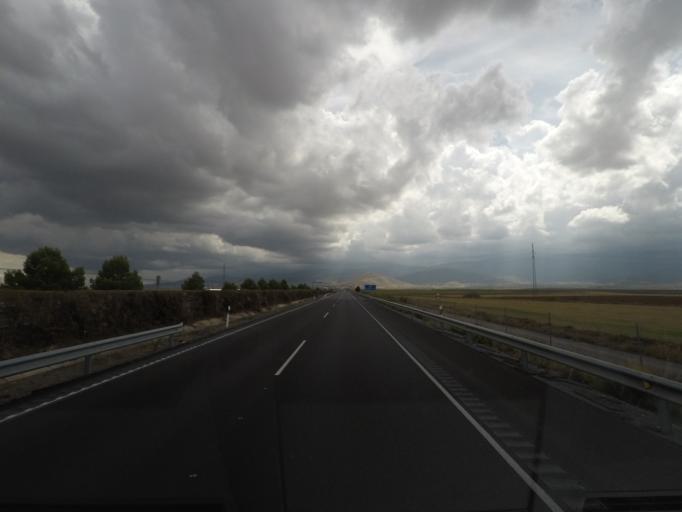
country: ES
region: Andalusia
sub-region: Provincia de Granada
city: Albunan
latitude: 37.2251
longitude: -3.0803
